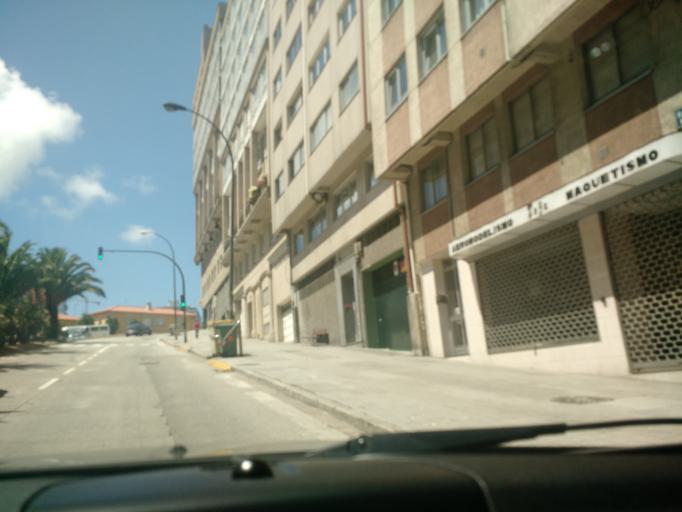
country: ES
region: Galicia
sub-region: Provincia da Coruna
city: A Coruna
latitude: 43.3585
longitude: -8.4087
